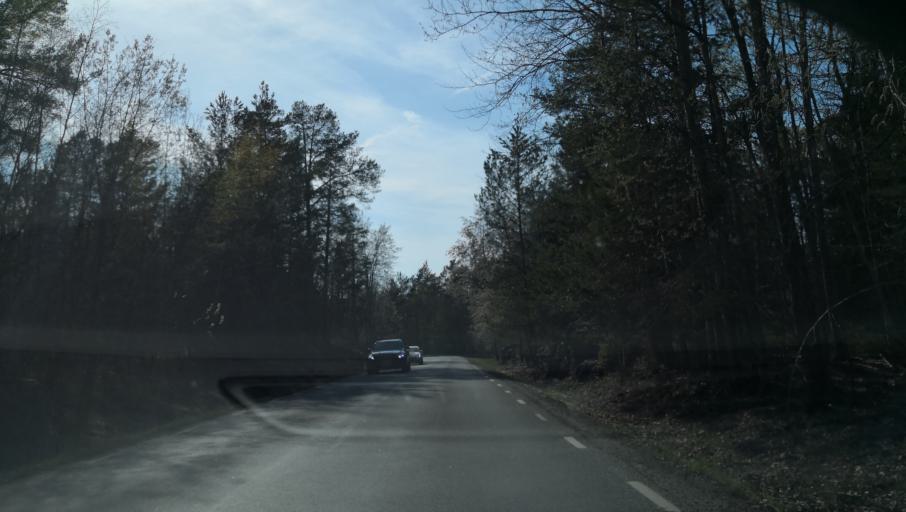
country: SE
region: Stockholm
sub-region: Varmdo Kommun
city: Holo
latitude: 59.3023
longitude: 18.6204
